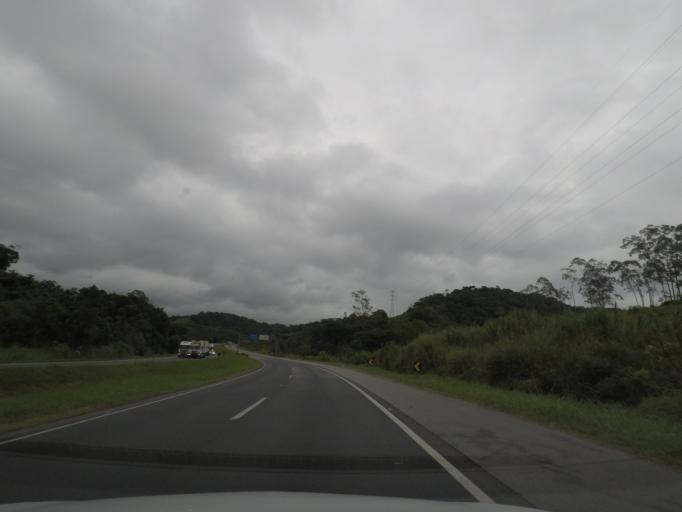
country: BR
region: Sao Paulo
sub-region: Juquia
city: Juquia
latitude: -24.3720
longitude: -47.7062
